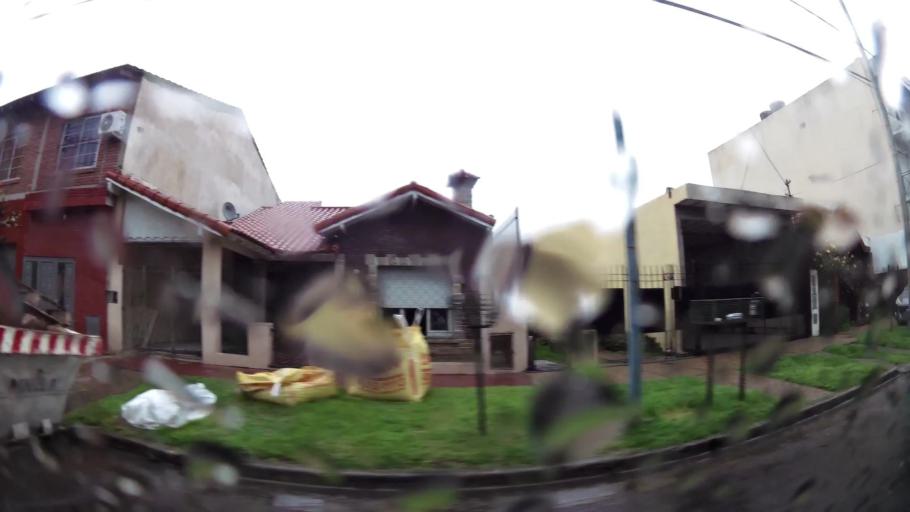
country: AR
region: Buenos Aires
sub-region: Partido de Lanus
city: Lanus
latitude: -34.7058
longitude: -58.4125
